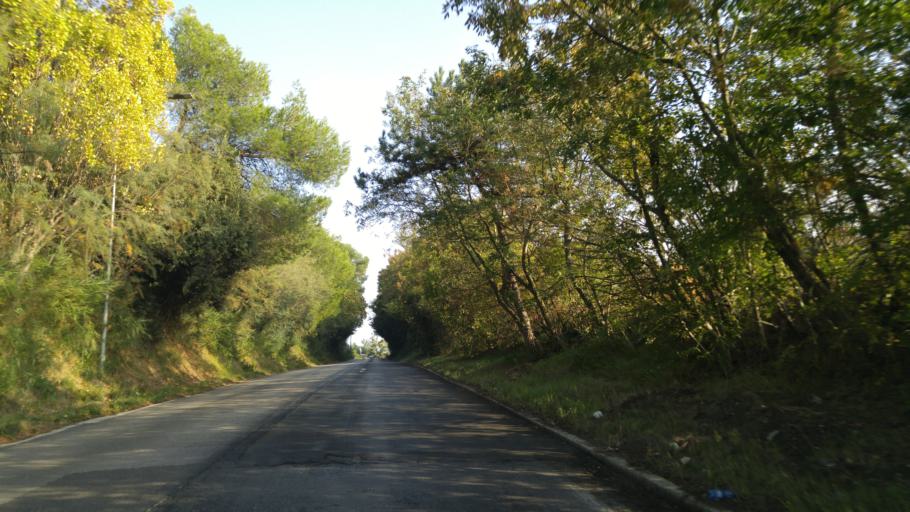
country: IT
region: The Marches
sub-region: Provincia di Pesaro e Urbino
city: Pesaro
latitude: 43.8912
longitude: 12.9456
